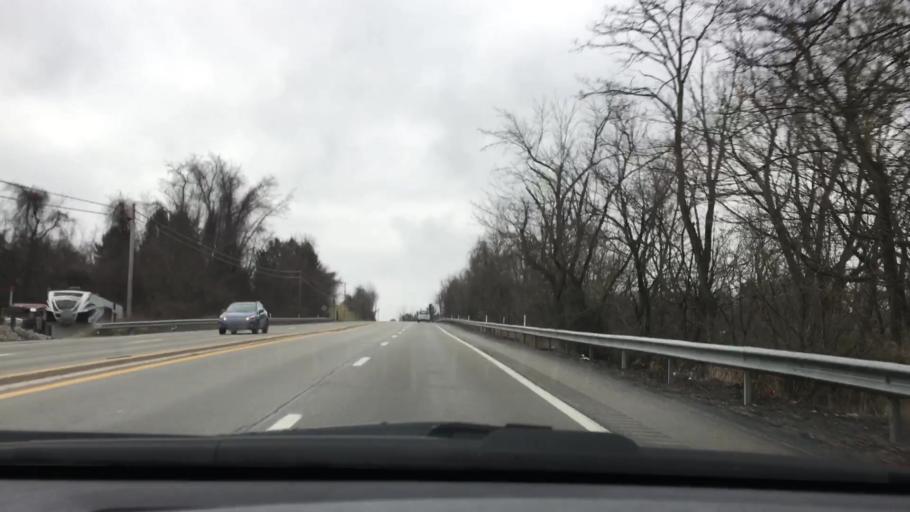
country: US
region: Pennsylvania
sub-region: Fayette County
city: Perryopolis
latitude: 40.1175
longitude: -79.7719
